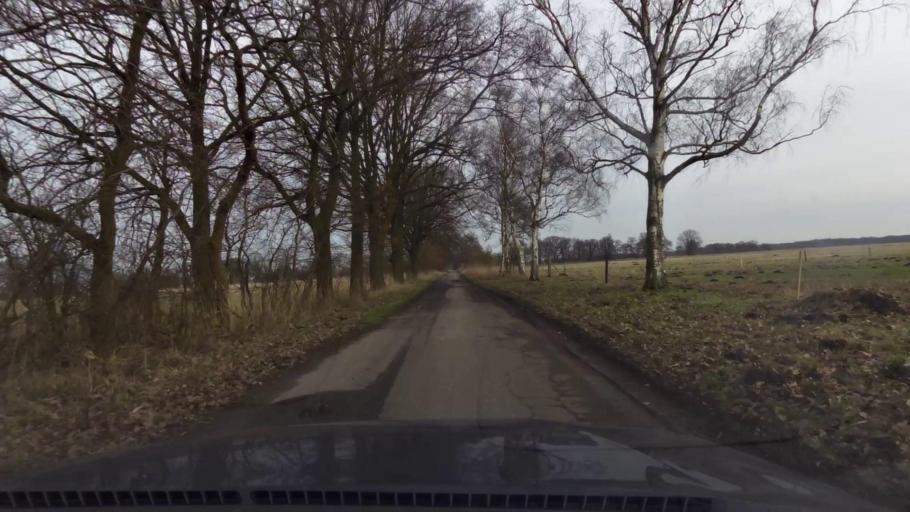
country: PL
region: West Pomeranian Voivodeship
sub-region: Powiat goleniowski
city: Stepnica
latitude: 53.7259
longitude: 14.5559
